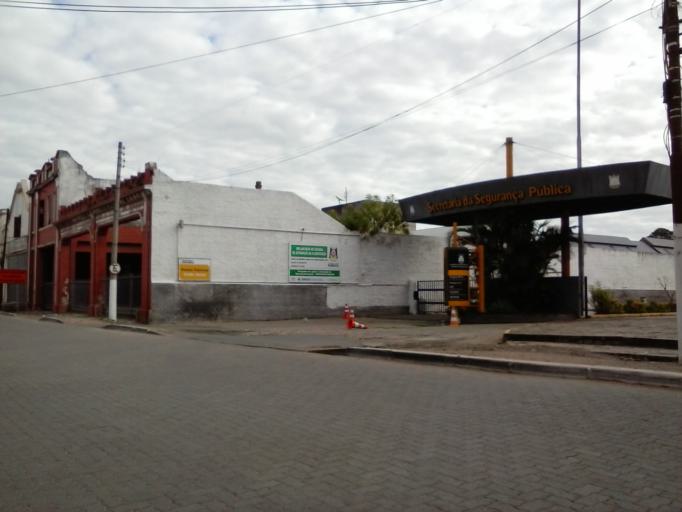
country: BR
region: Rio Grande do Sul
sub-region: Porto Alegre
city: Porto Alegre
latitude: -30.0222
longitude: -51.2155
